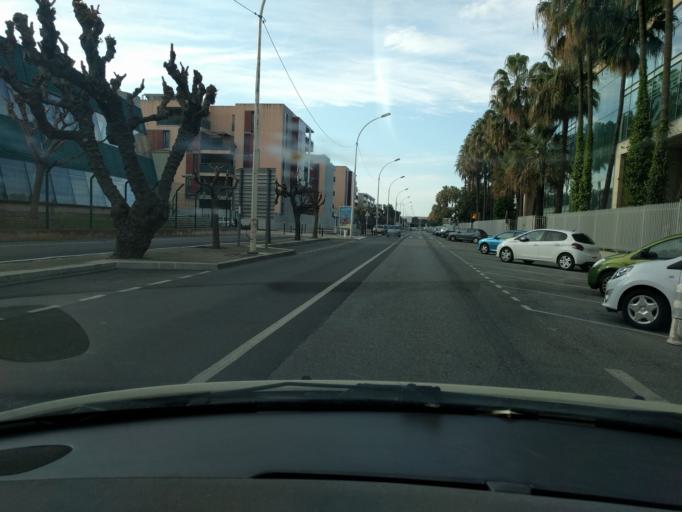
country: FR
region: Provence-Alpes-Cote d'Azur
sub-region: Departement des Alpes-Maritimes
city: Mandelieu-la-Napoule
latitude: 43.5535
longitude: 6.9659
